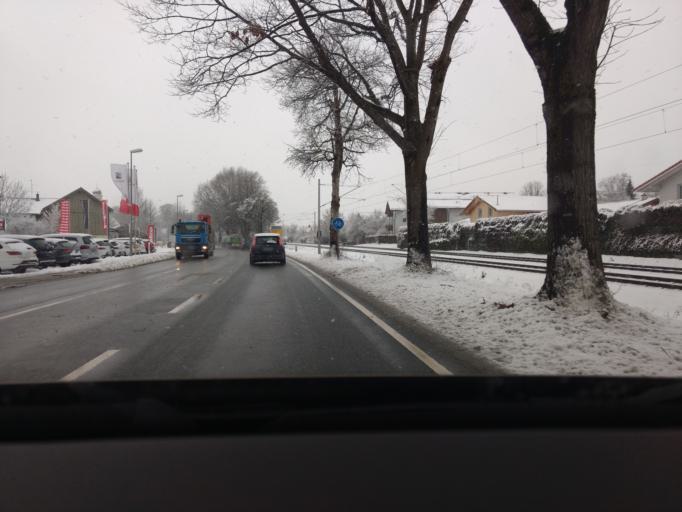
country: DE
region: Bavaria
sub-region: Upper Bavaria
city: Traunstein
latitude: 47.8643
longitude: 12.6289
